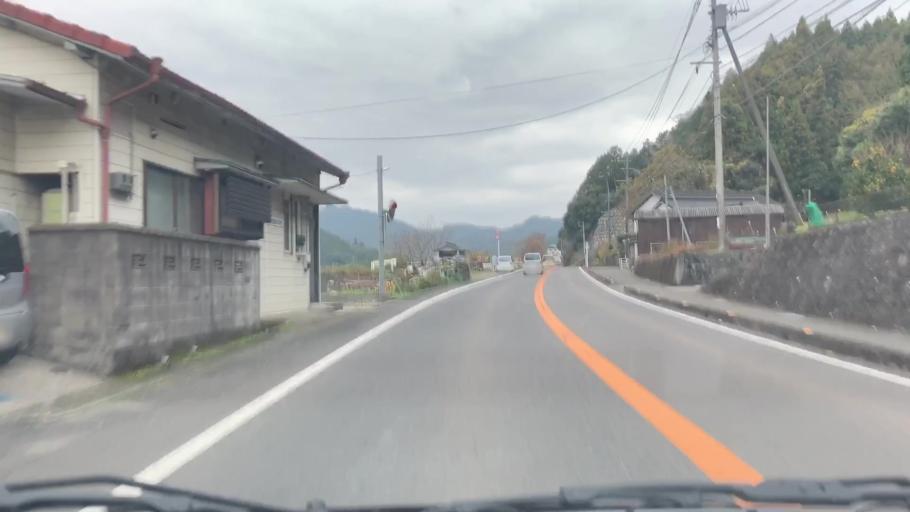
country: JP
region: Saga Prefecture
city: Ureshinomachi-shimojuku
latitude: 33.1277
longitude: 130.0363
